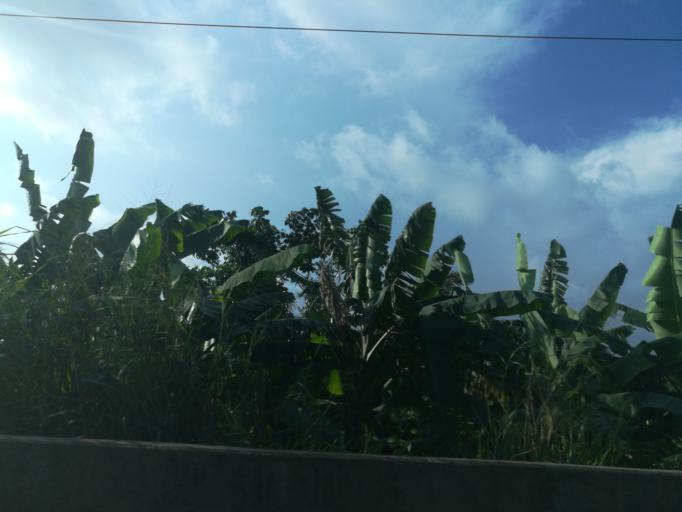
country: NG
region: Ogun
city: Ado Odo
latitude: 6.4905
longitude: 3.0745
